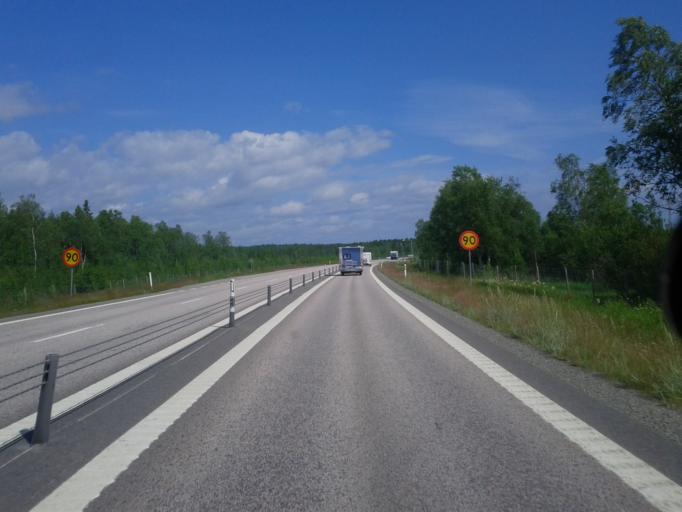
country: SE
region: Vaesterbotten
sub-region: Nordmalings Kommun
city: Nordmaling
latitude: 63.5704
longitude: 19.4375
